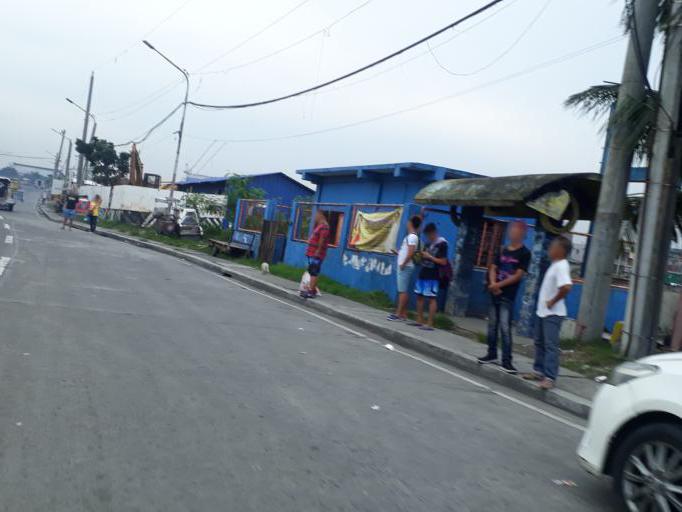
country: PH
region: Metro Manila
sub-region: Caloocan City
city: Niugan
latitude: 14.6535
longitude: 120.9545
